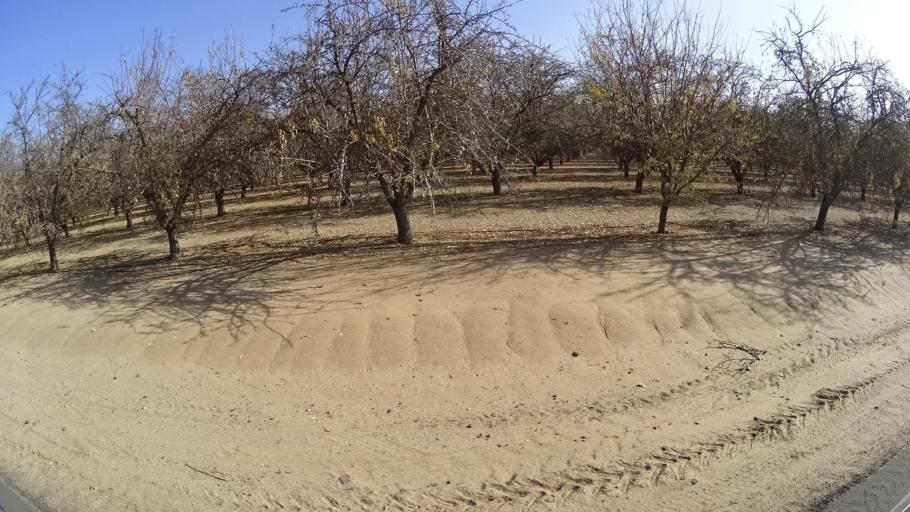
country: US
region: California
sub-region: Kern County
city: McFarland
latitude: 35.6373
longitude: -119.1867
